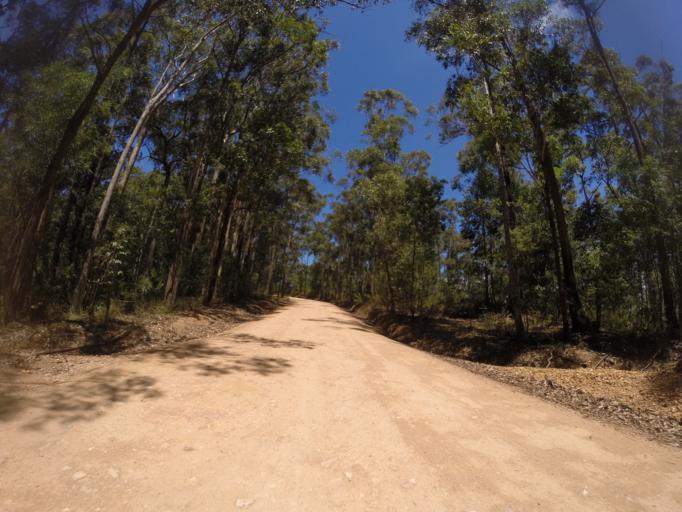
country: AU
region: New South Wales
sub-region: Shoalhaven Shire
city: Ulladulla
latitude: -35.5075
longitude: 150.2981
